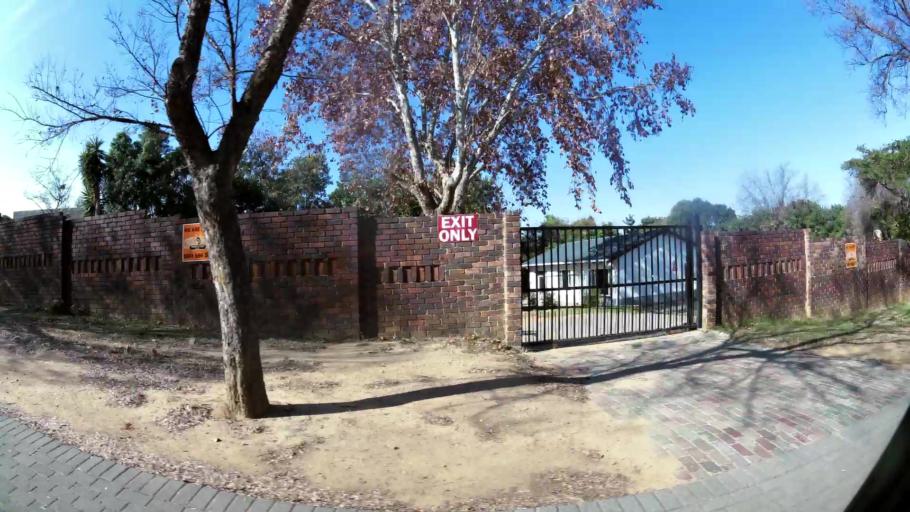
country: ZA
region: Gauteng
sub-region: City of Johannesburg Metropolitan Municipality
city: Roodepoort
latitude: -26.0983
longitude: 27.9521
